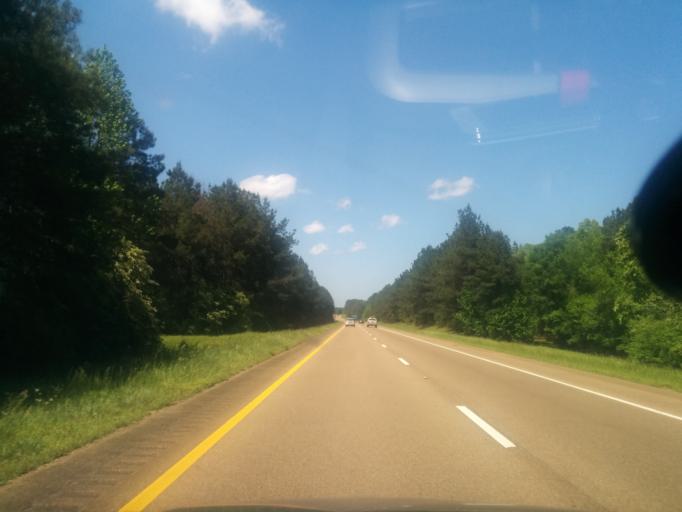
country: US
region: Mississippi
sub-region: Lincoln County
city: Brookhaven
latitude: 31.5254
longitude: -90.4790
